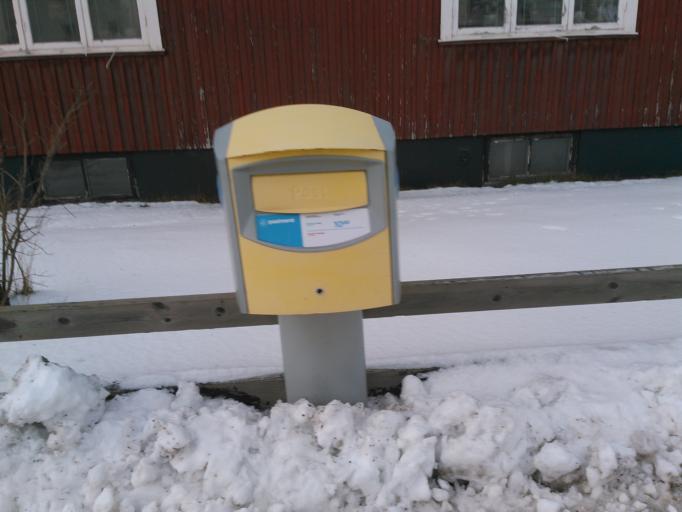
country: SE
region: Vaesterbotten
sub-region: Umea Kommun
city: Umea
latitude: 63.8308
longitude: 20.2331
